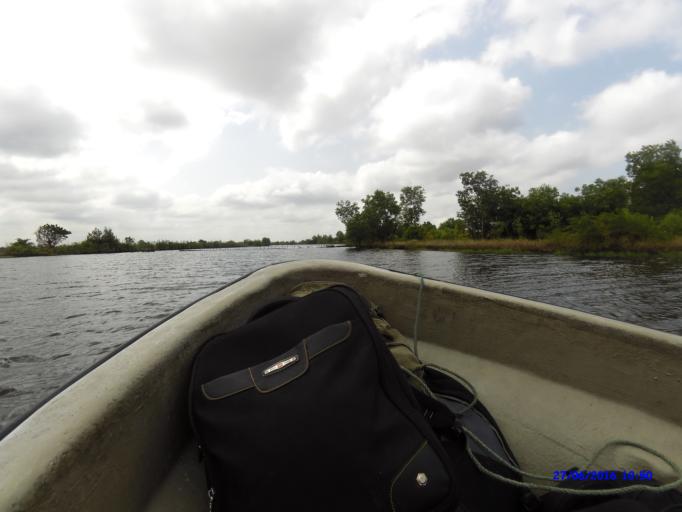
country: BJ
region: Mono
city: Come
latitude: 6.3685
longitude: 1.9285
